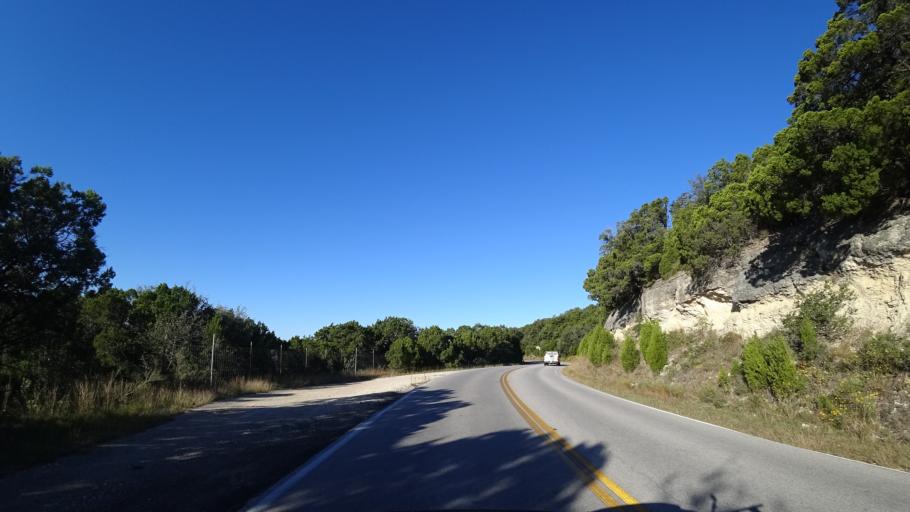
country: US
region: Texas
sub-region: Travis County
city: West Lake Hills
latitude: 30.3626
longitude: -97.8149
